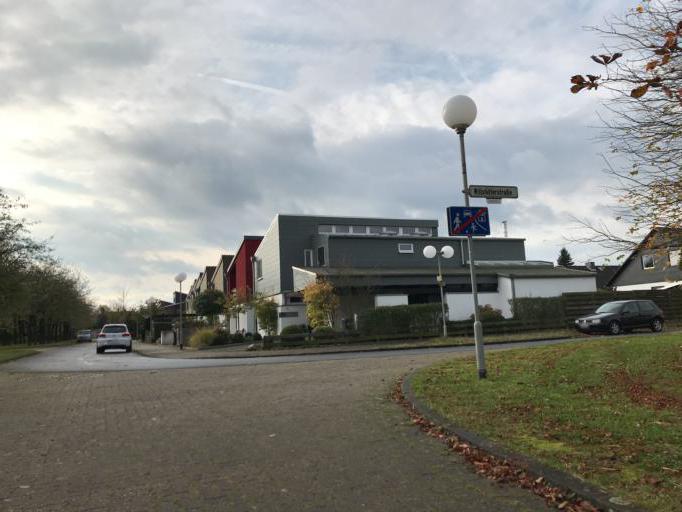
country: DE
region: Lower Saxony
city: Klein Schwulper
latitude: 52.2885
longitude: 10.4626
